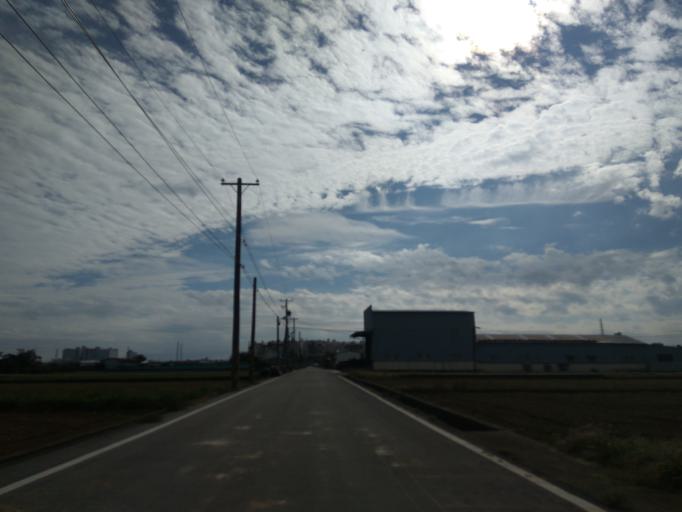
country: TW
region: Taiwan
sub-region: Hsinchu
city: Zhubei
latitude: 24.9895
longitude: 121.0909
